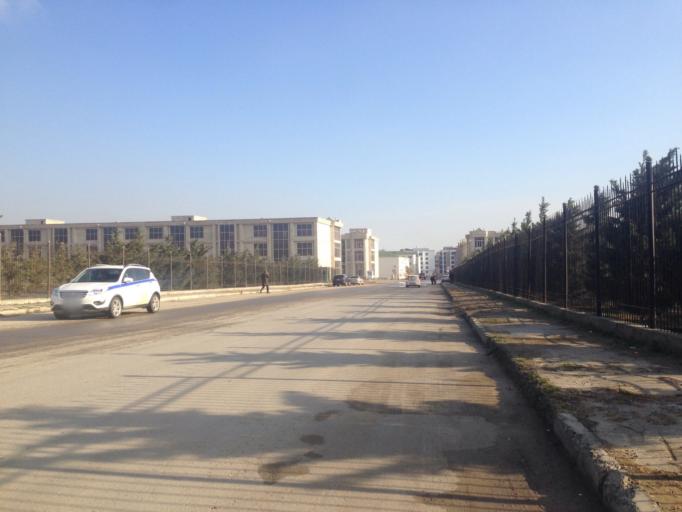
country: AZ
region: Baki
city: Baku
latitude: 40.4093
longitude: 49.8568
